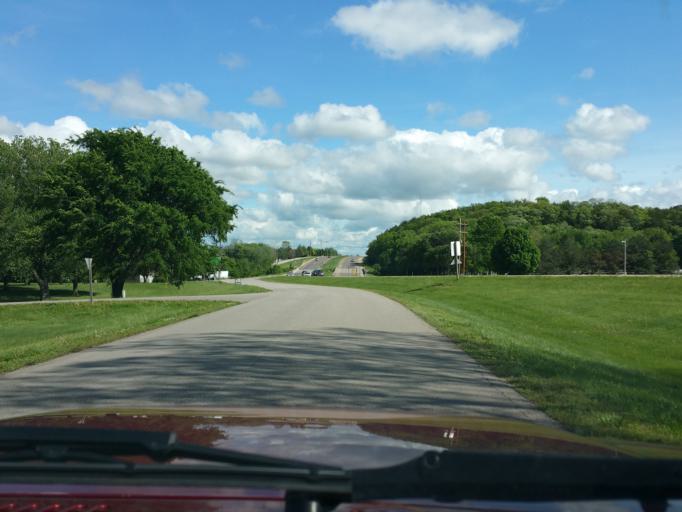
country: US
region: Kansas
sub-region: Riley County
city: Manhattan
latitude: 39.2469
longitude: -96.5972
